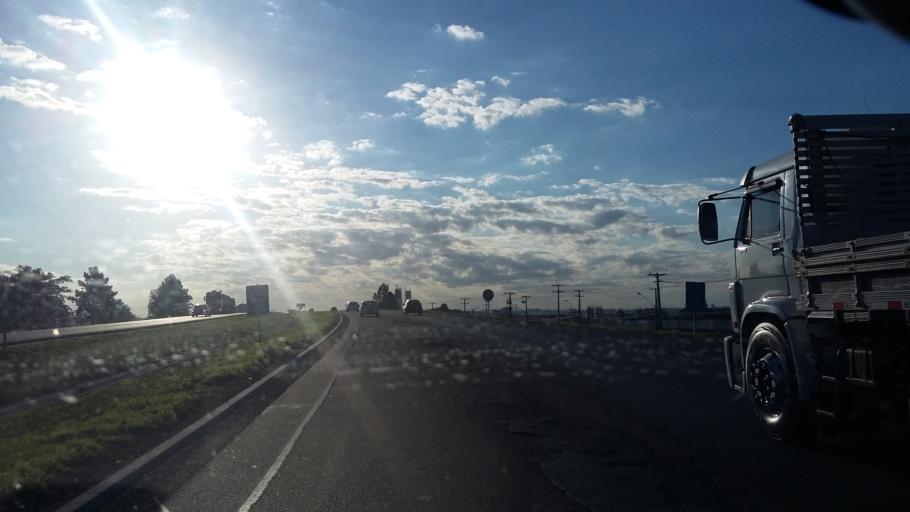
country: BR
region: Parana
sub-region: Sao Jose Dos Pinhais
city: Sao Jose dos Pinhais
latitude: -25.5363
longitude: -49.3148
